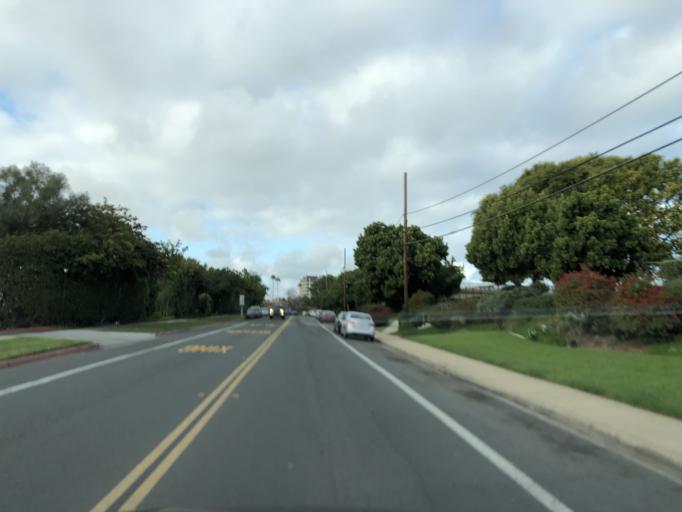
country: US
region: California
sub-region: San Diego County
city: La Jolla
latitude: 32.8141
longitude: -117.1821
